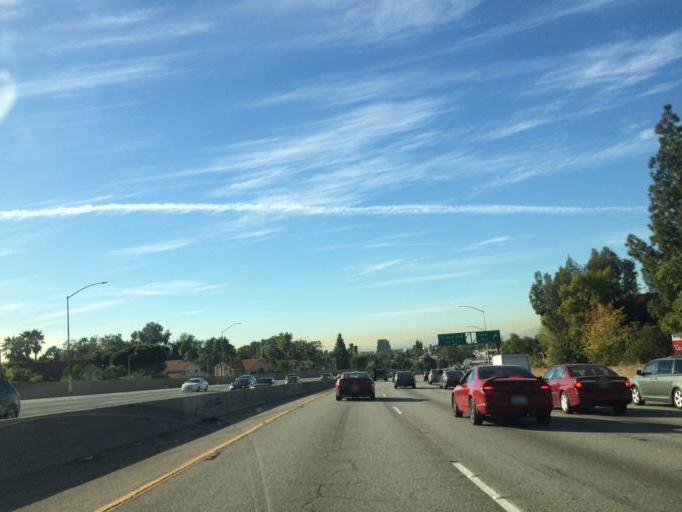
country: US
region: California
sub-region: Los Angeles County
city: Charter Oak
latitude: 34.0682
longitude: -117.8593
